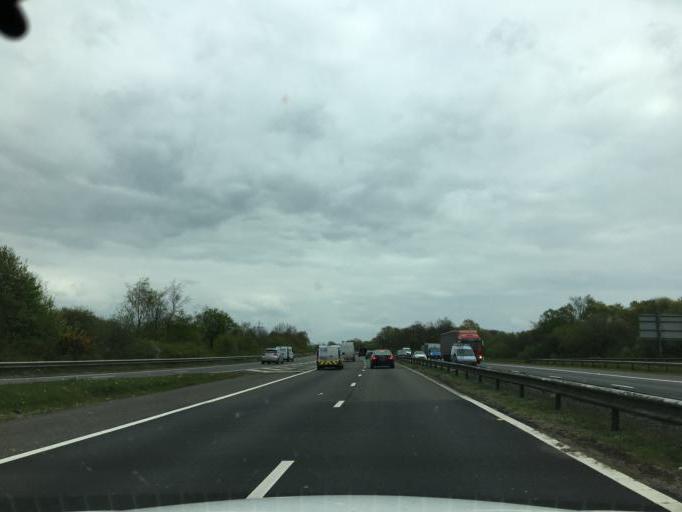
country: GB
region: Wales
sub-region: City and County of Swansea
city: Morriston
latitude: 51.6759
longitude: -3.9538
